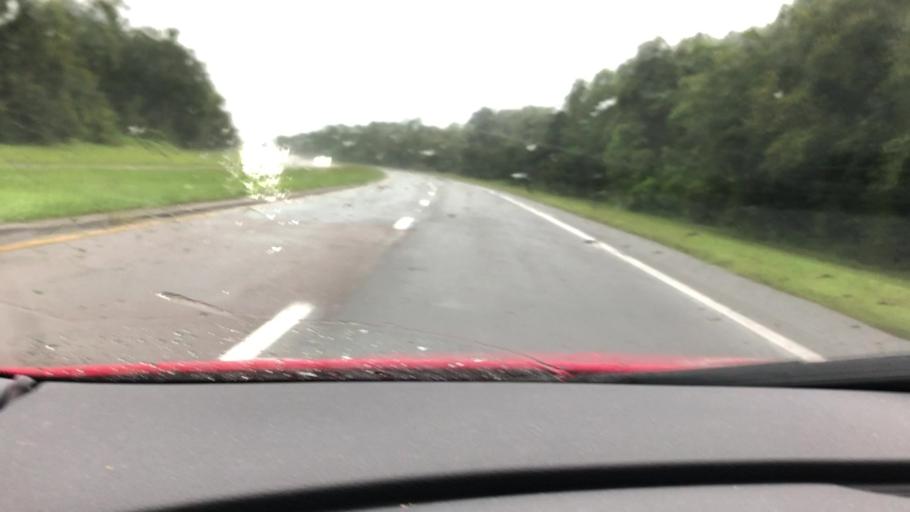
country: US
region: Florida
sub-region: Volusia County
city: Lake Helen
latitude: 29.0151
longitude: -81.2425
